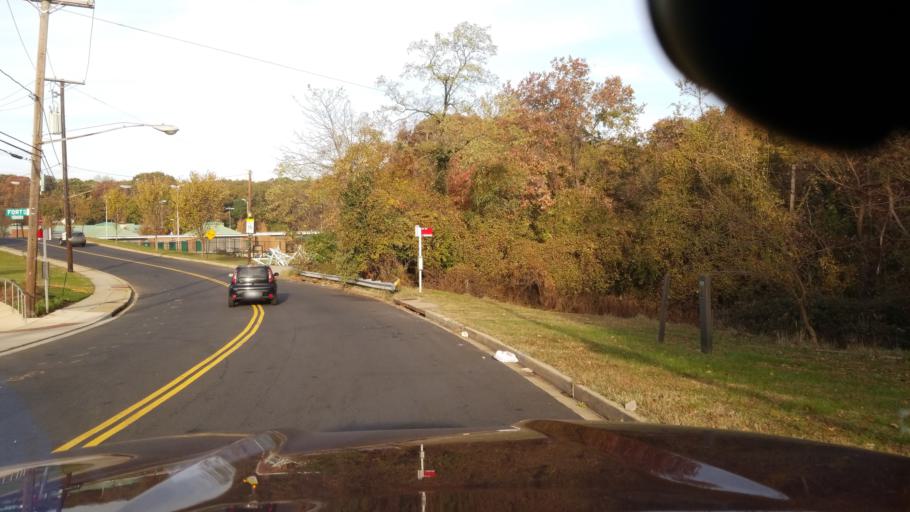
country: US
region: Maryland
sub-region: Prince George's County
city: Hillcrest Heights
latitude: 38.8571
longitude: -76.9765
